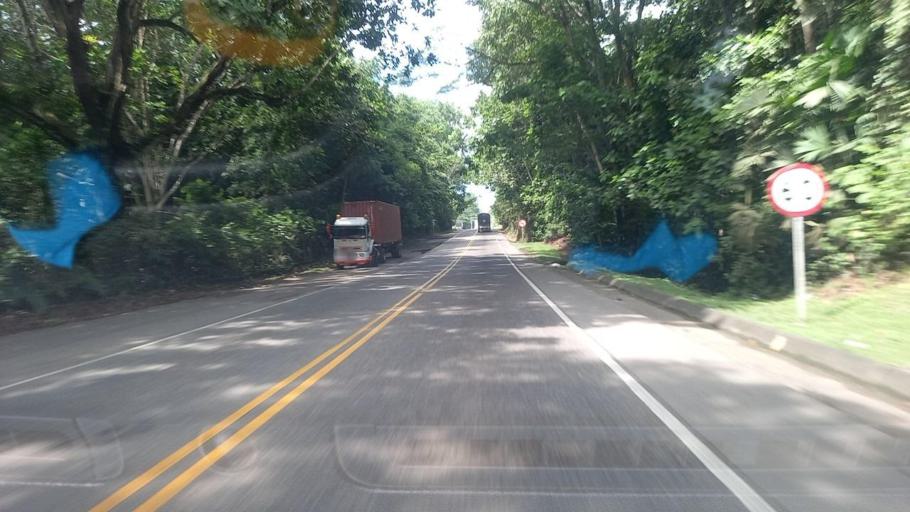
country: CO
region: Santander
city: Sabana de Torres
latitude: 7.1281
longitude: -73.5717
